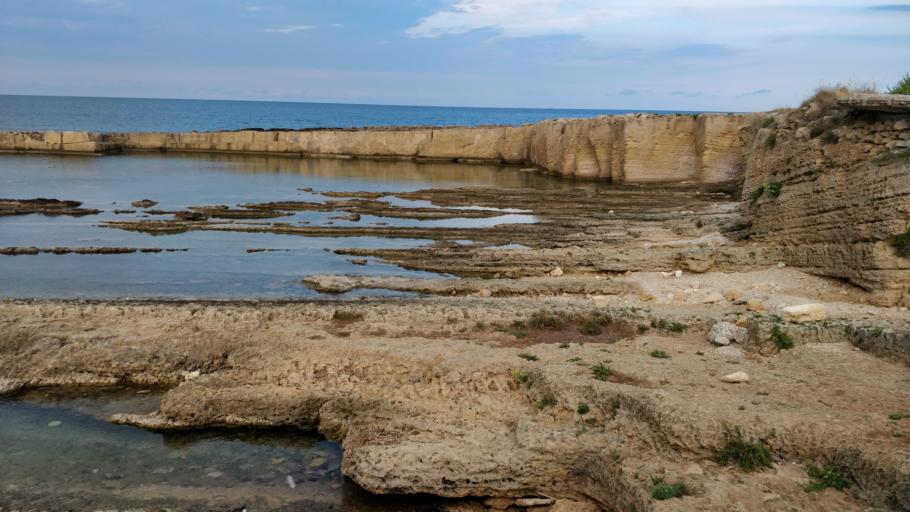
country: IT
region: Sicily
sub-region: Provincia di Siracusa
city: Carrozziere
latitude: 37.0408
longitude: 15.3071
